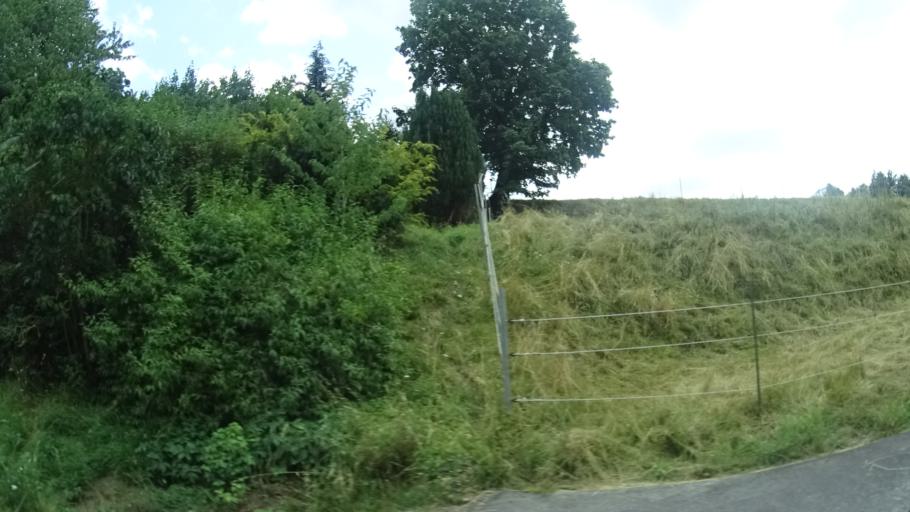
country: DE
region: Hesse
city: Gedern
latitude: 50.4218
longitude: 9.2450
